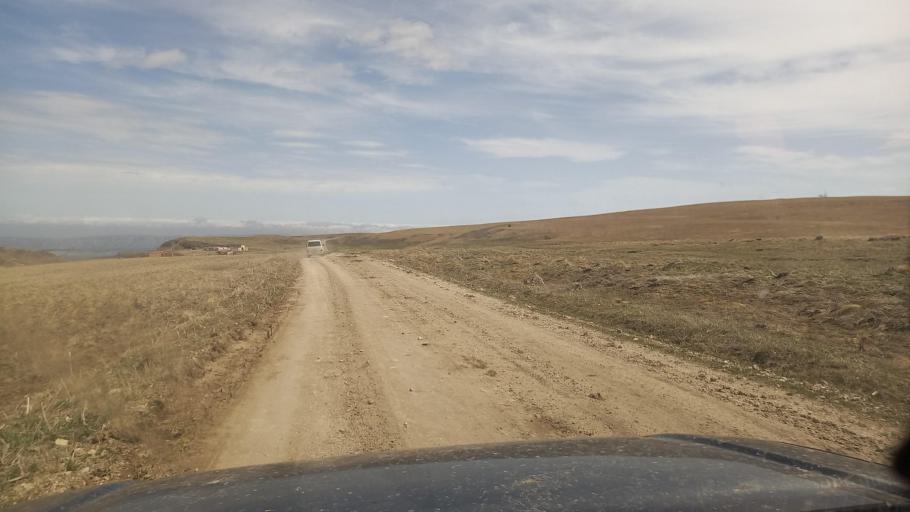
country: RU
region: Stavropol'skiy
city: Kislovodsk
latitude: 43.7460
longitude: 42.7008
